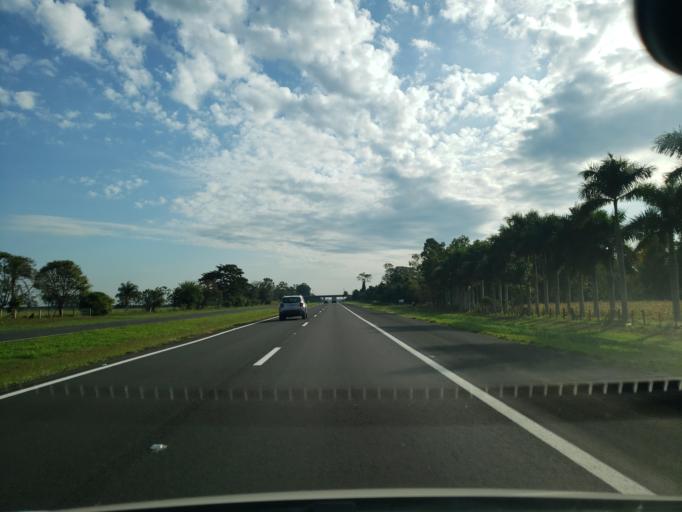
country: BR
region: Sao Paulo
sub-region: Guararapes
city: Guararapes
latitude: -21.2036
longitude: -50.6104
